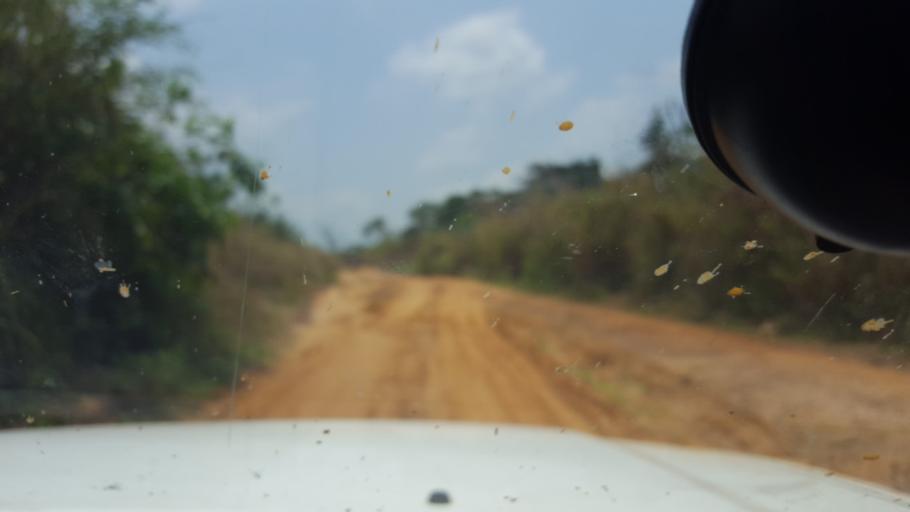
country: CD
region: Bandundu
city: Mushie
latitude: -3.7532
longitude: 16.6668
